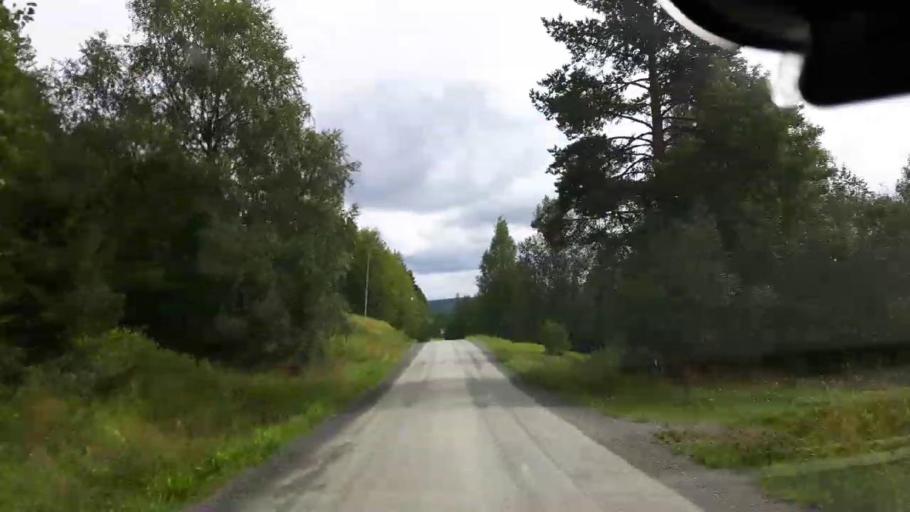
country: SE
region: Jaemtland
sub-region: Krokoms Kommun
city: Valla
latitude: 63.6187
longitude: 14.0665
